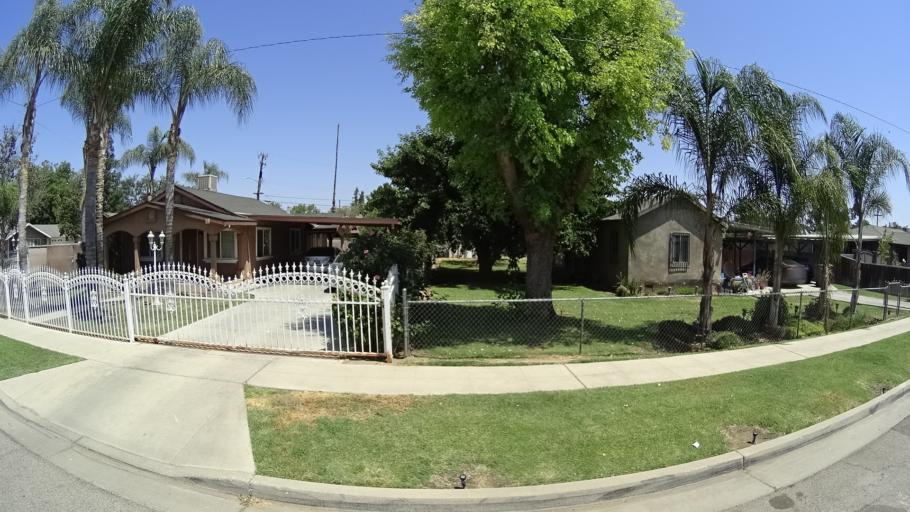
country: US
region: California
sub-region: Fresno County
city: West Park
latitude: 36.7078
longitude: -119.8107
